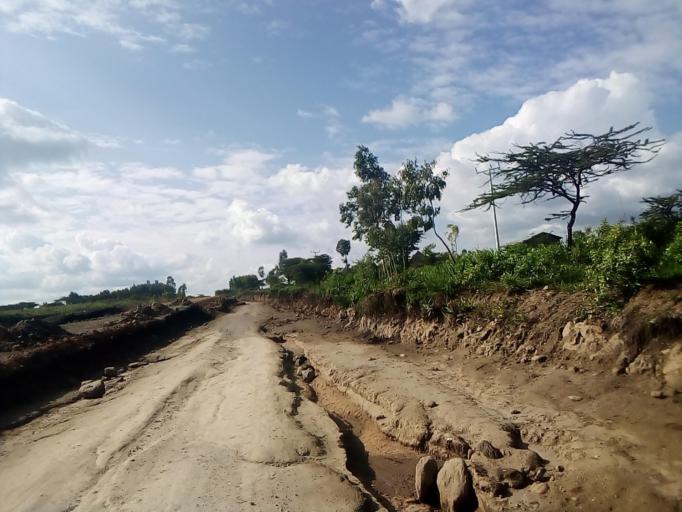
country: ET
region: Southern Nations, Nationalities, and People's Region
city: K'olito
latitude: 7.6306
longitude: 38.0628
